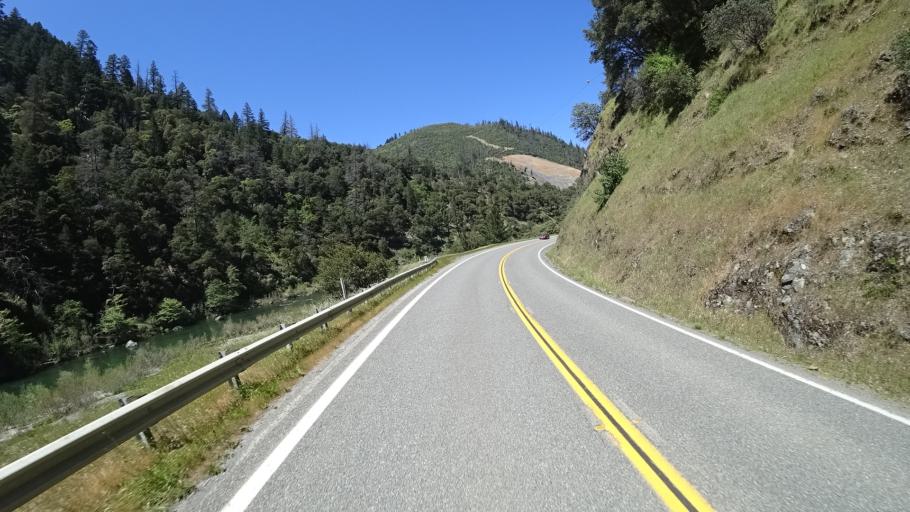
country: US
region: California
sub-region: Trinity County
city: Hayfork
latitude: 40.7734
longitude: -123.3116
